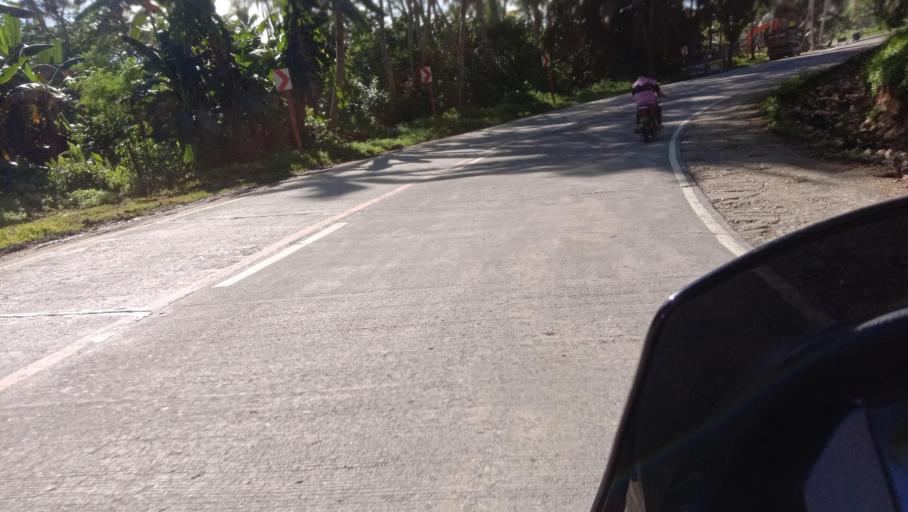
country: PH
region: Caraga
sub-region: Province of Surigao del Sur
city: Barobo
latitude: 8.5382
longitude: 126.0974
